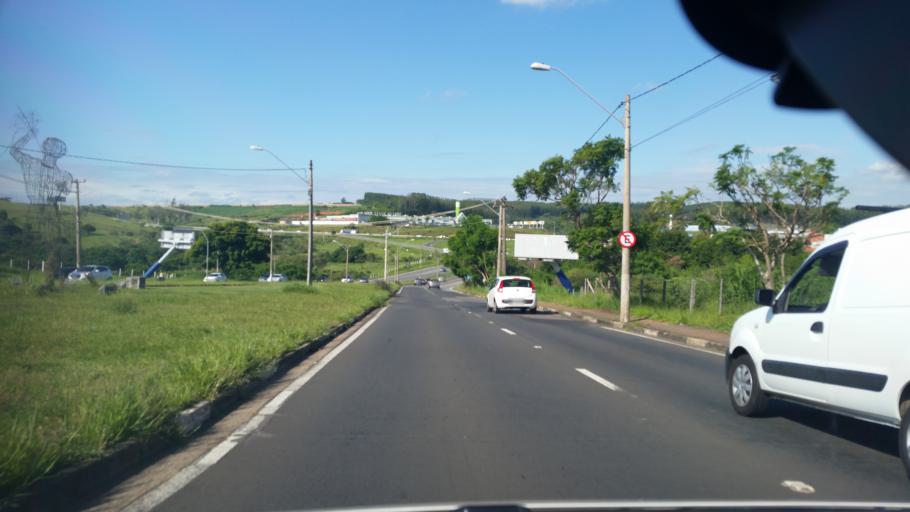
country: BR
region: Sao Paulo
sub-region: Campinas
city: Campinas
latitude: -22.8890
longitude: -47.0175
